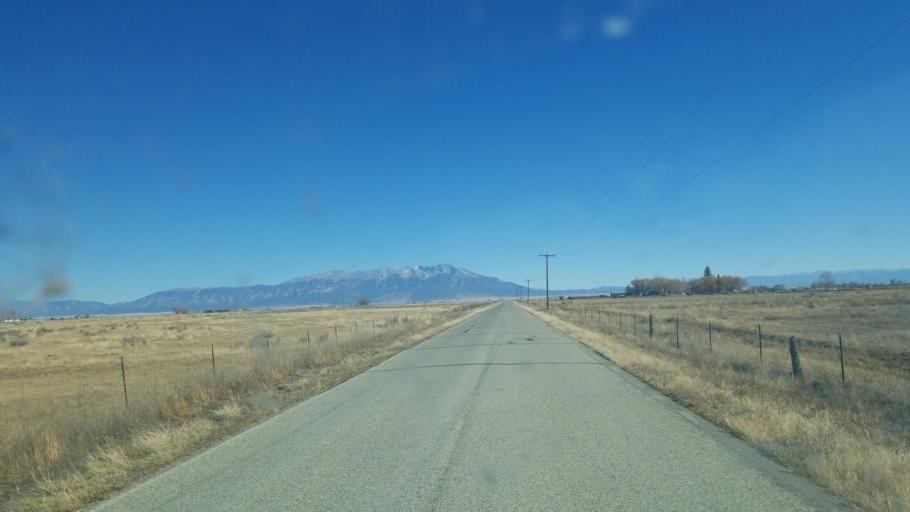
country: US
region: Colorado
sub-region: Alamosa County
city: Alamosa
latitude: 37.5309
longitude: -105.9014
